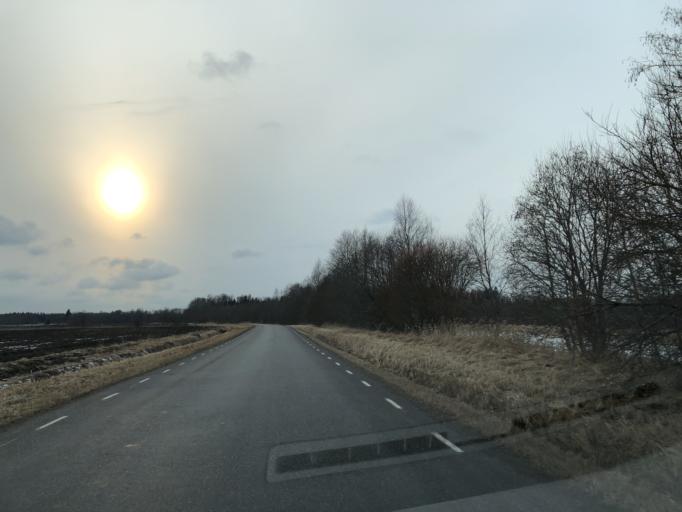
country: EE
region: Paernumaa
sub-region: Vaendra vald (alev)
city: Vandra
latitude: 58.6947
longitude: 24.9535
